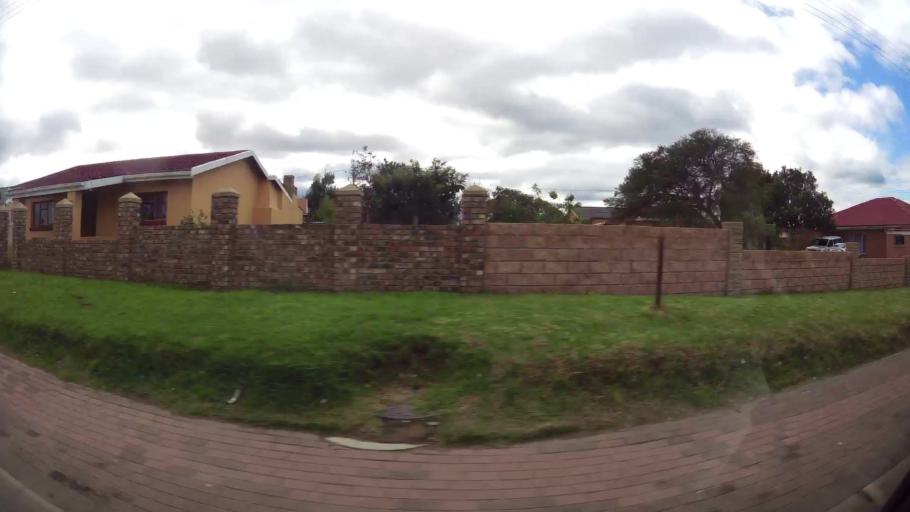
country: ZA
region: Western Cape
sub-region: Eden District Municipality
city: George
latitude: -34.0176
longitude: 22.4637
